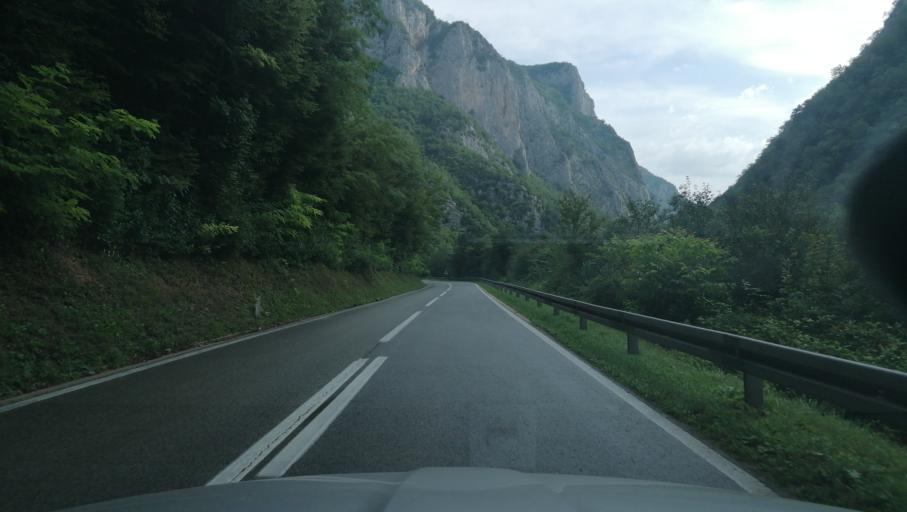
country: BA
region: Republika Srpska
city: Hiseti
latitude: 44.6783
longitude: 17.1669
